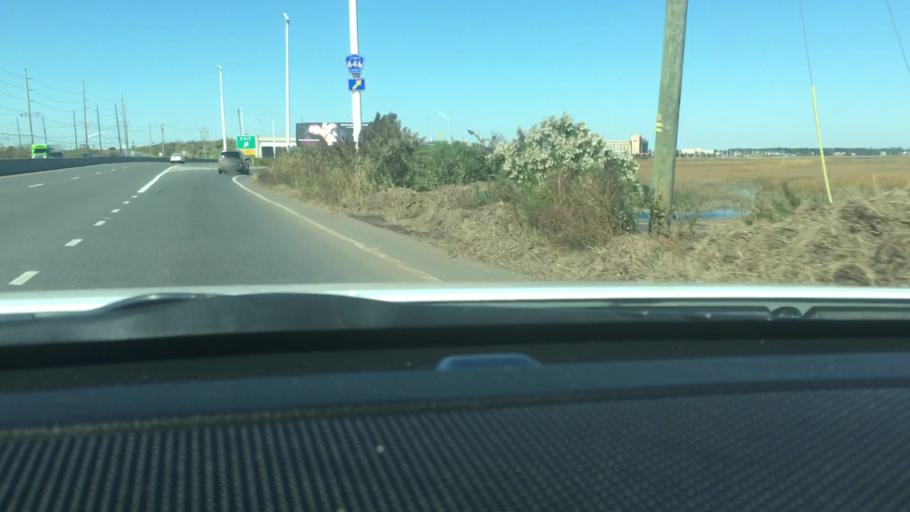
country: US
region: New Jersey
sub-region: Atlantic County
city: Pleasantville
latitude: 39.3936
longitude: -74.4906
